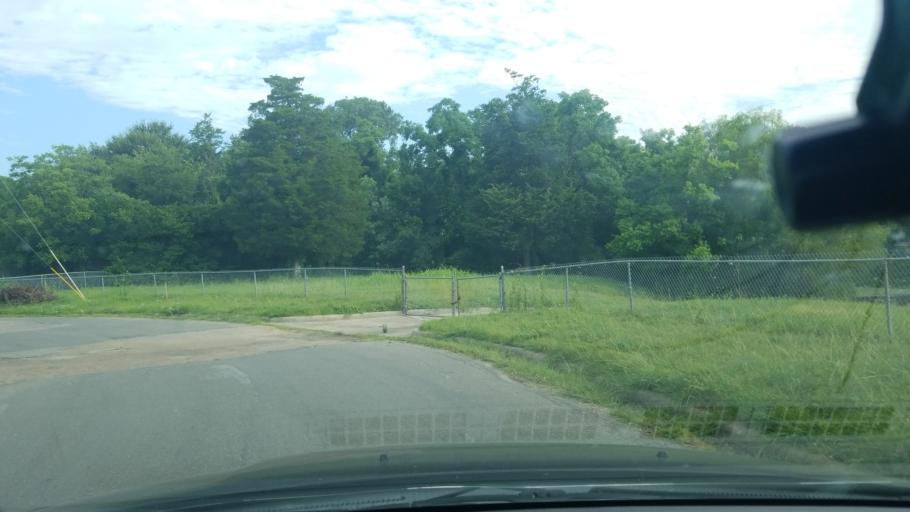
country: US
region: Texas
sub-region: Dallas County
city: Balch Springs
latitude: 32.7403
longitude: -96.6687
